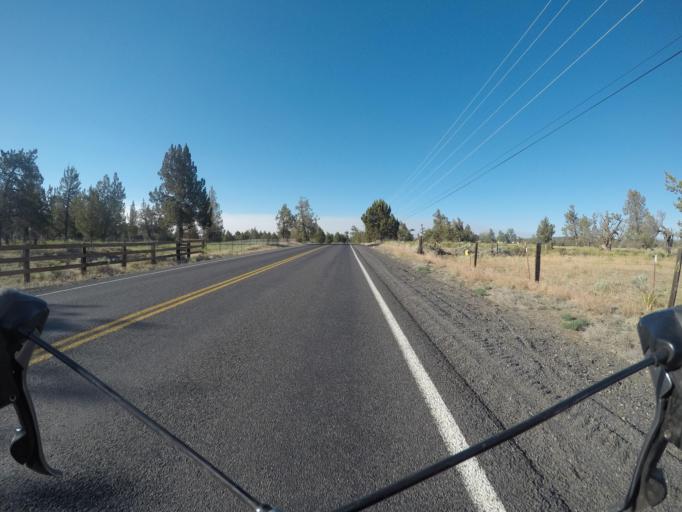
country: US
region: Oregon
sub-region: Deschutes County
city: Redmond
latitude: 44.1999
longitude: -121.2436
